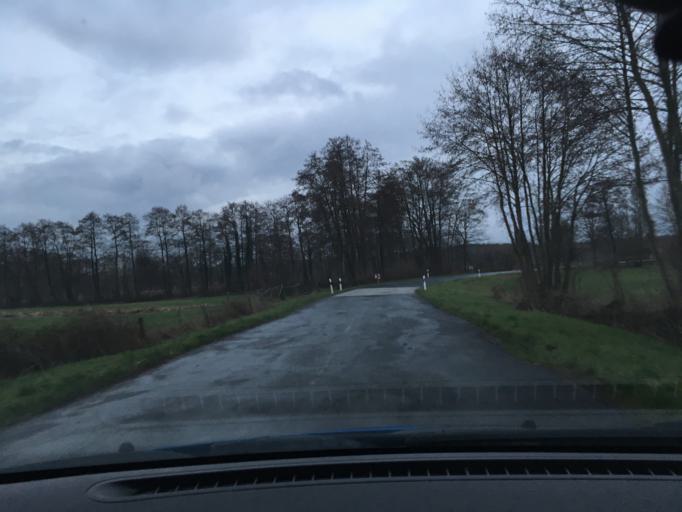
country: DE
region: Mecklenburg-Vorpommern
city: Nostorf
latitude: 53.4030
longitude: 10.6673
